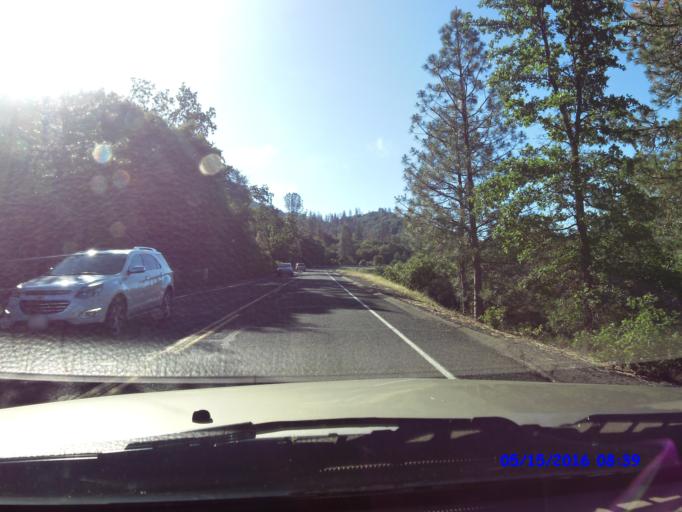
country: US
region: California
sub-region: Madera County
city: Ahwahnee
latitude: 37.4379
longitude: -119.7363
